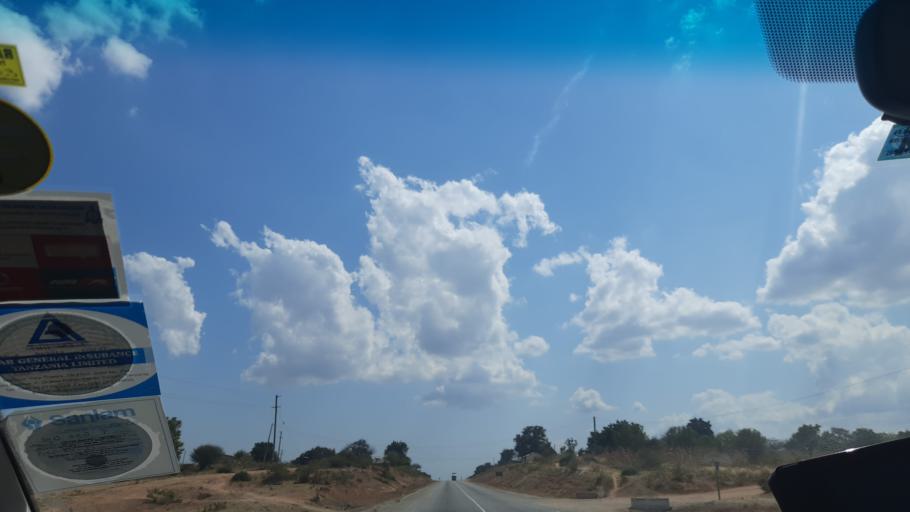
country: TZ
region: Singida
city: Kintinku
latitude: -6.0146
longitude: 35.4382
